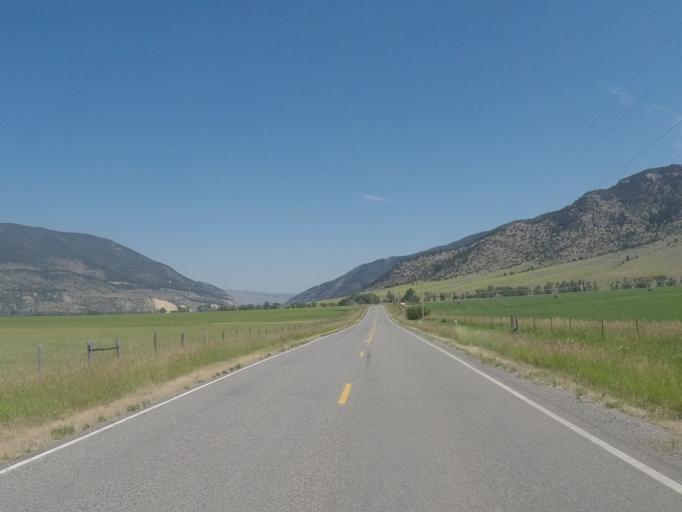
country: US
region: Montana
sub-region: Park County
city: Livingston
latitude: 45.5600
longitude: -110.5589
